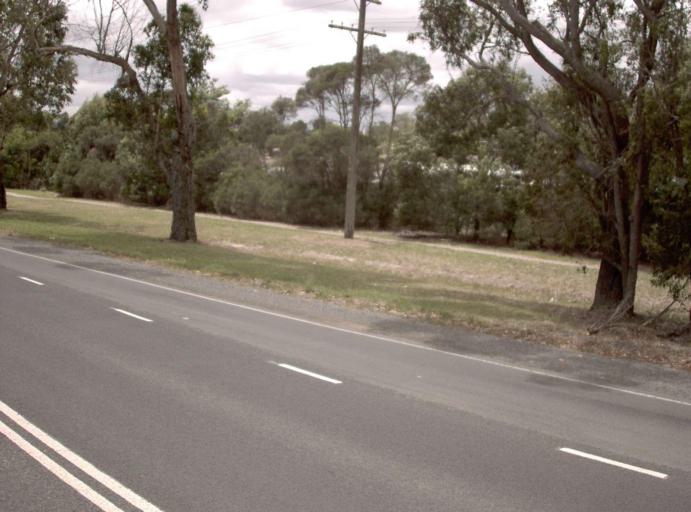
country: AU
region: Victoria
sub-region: Yarra Ranges
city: Lilydale
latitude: -37.7284
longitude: 145.3778
